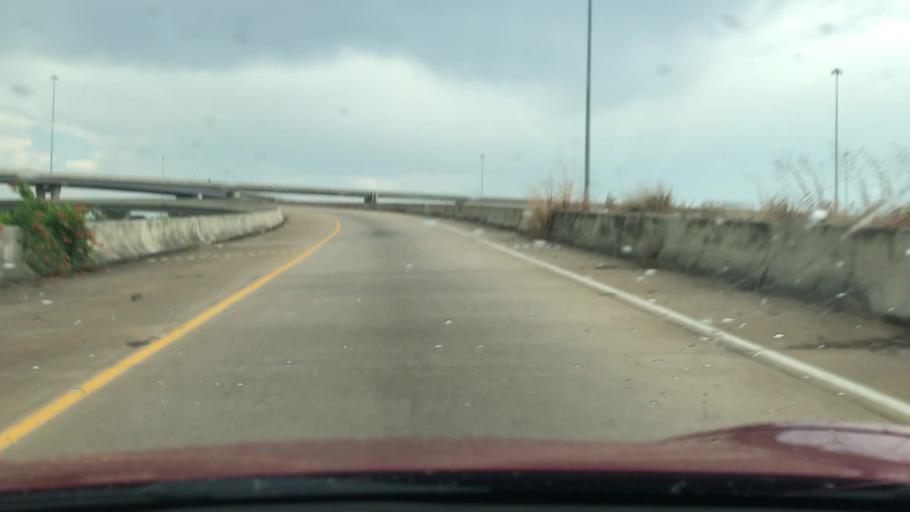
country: US
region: Louisiana
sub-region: Bossier Parish
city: Bossier City
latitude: 32.4188
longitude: -93.7530
